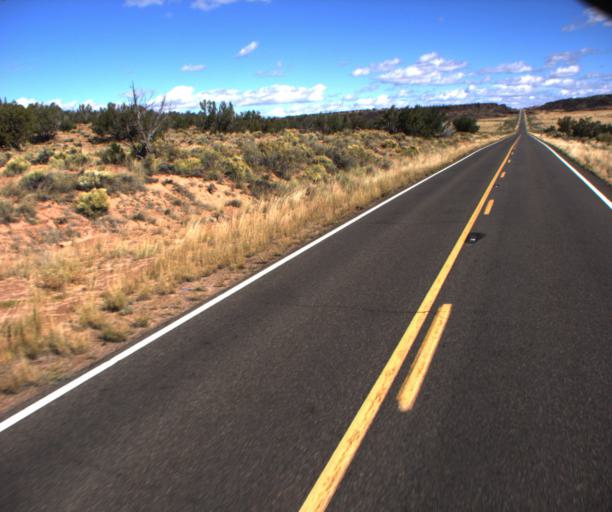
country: US
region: Arizona
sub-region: Apache County
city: Saint Johns
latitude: 34.7360
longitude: -109.2514
